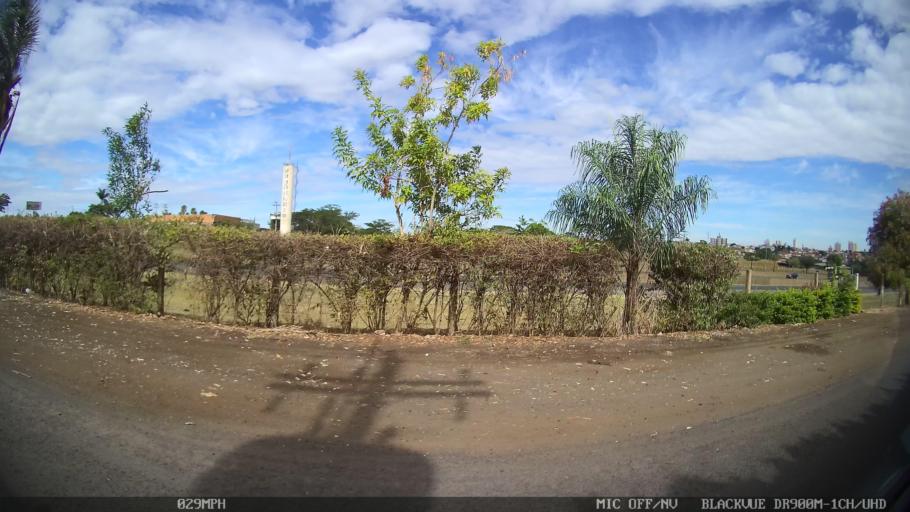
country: BR
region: Sao Paulo
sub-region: Sao Jose Do Rio Preto
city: Sao Jose do Rio Preto
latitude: -20.8097
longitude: -49.4948
